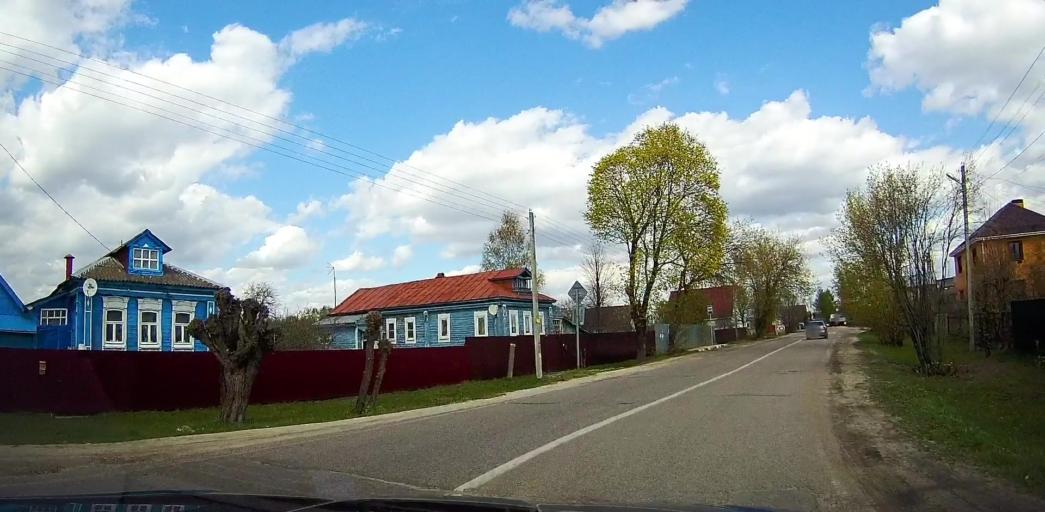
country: RU
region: Moskovskaya
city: Davydovo
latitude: 55.6047
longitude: 38.8466
